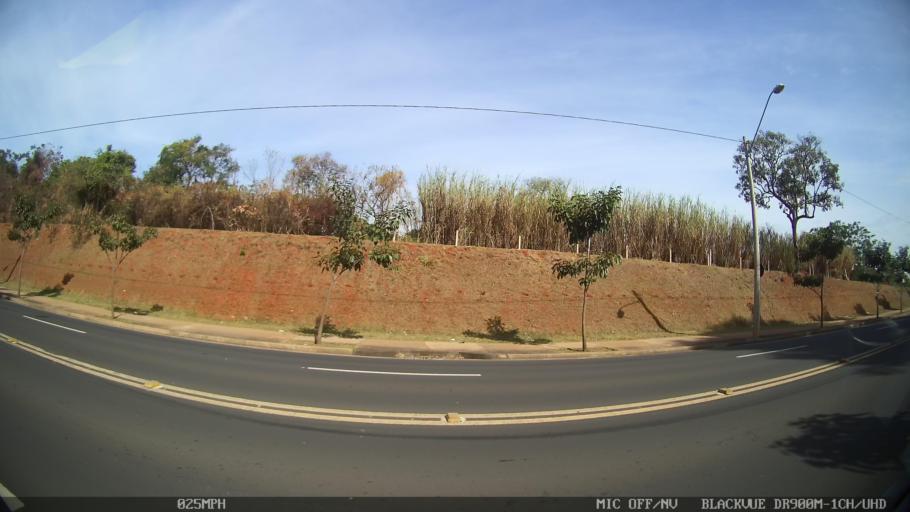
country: BR
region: Sao Paulo
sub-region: Piracicaba
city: Piracicaba
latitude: -22.7473
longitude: -47.6241
